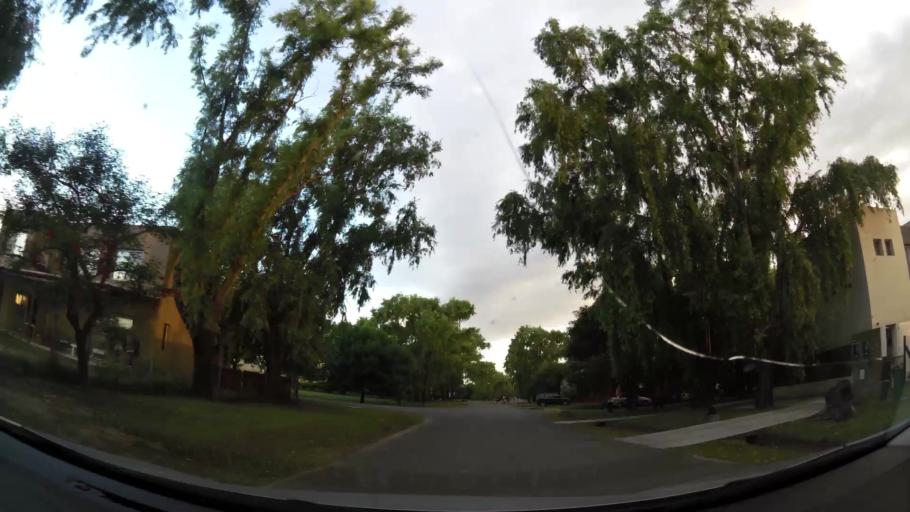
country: AR
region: Buenos Aires
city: Santa Catalina - Dique Lujan
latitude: -34.4397
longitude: -58.6571
